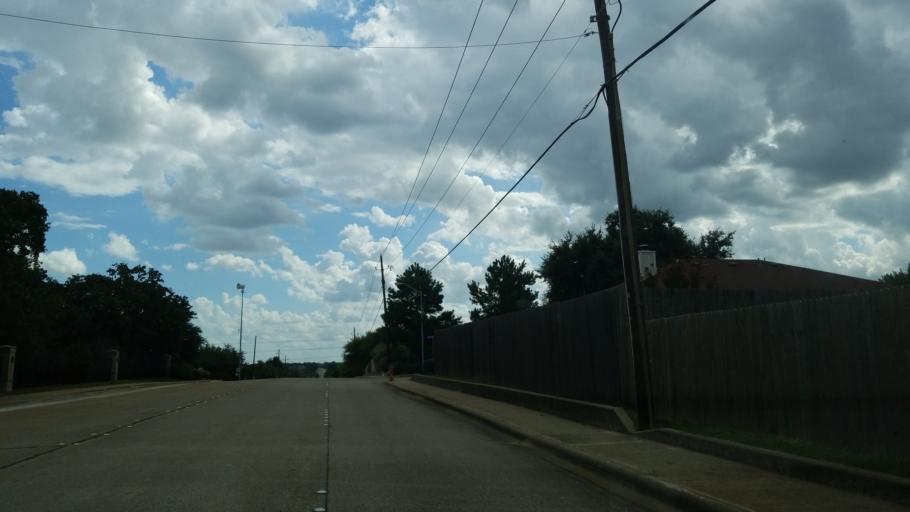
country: US
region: Texas
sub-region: Tarrant County
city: Euless
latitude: 32.8735
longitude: -97.0738
